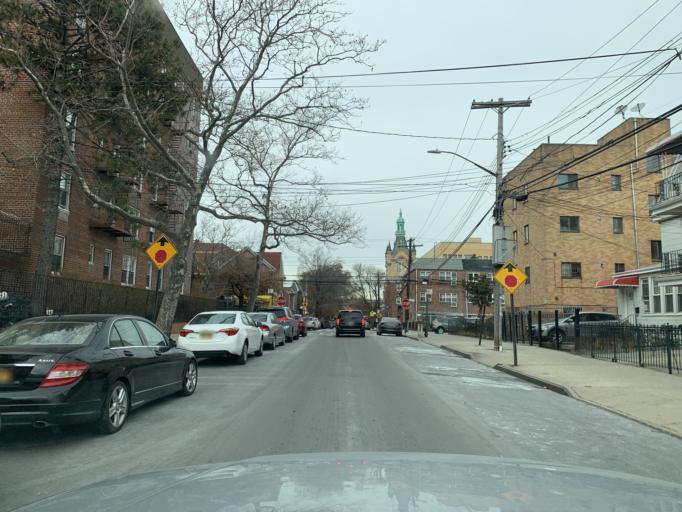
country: US
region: New York
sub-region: Queens County
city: Borough of Queens
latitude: 40.7391
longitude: -73.8739
